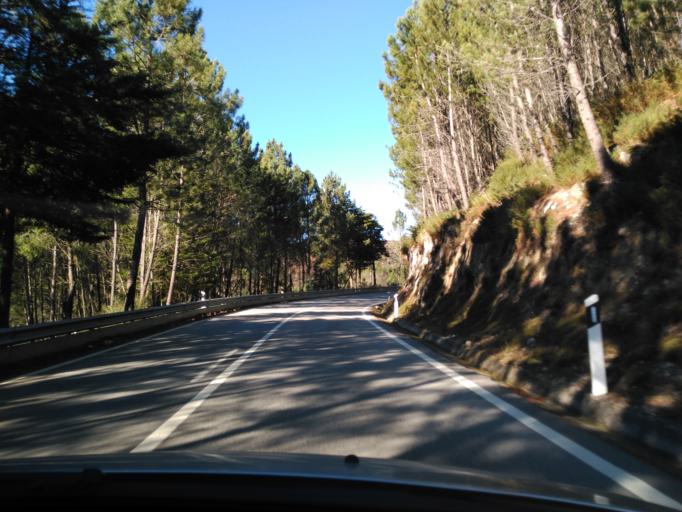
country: PT
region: Braga
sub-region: Cabeceiras de Basto
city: Cabeceiras de Basto
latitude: 41.6691
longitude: -7.9827
